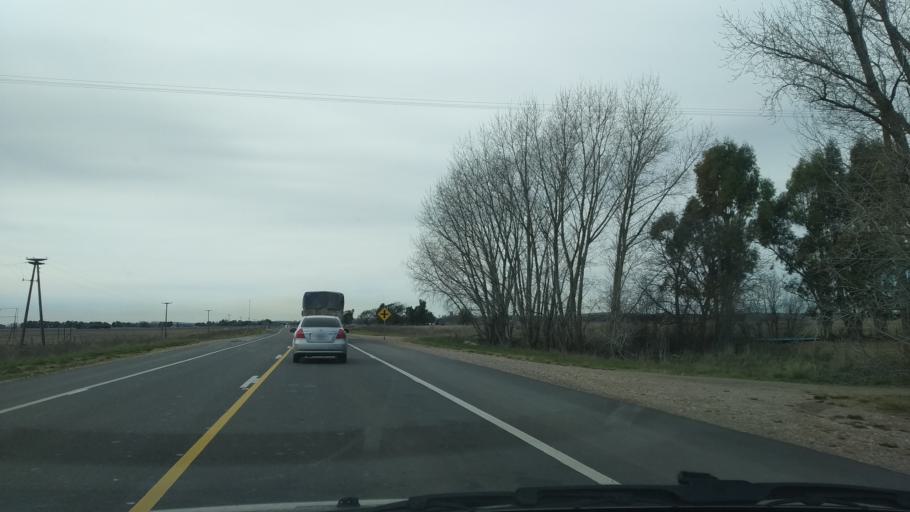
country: AR
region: Buenos Aires
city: Olavarria
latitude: -36.9982
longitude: -60.3428
